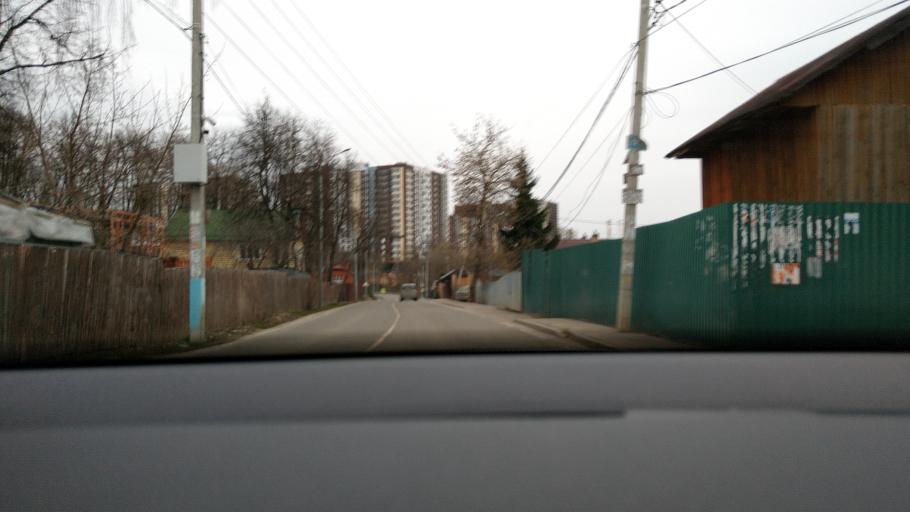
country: RU
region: Moskovskaya
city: Mosrentgen
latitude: 55.5951
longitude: 37.4432
